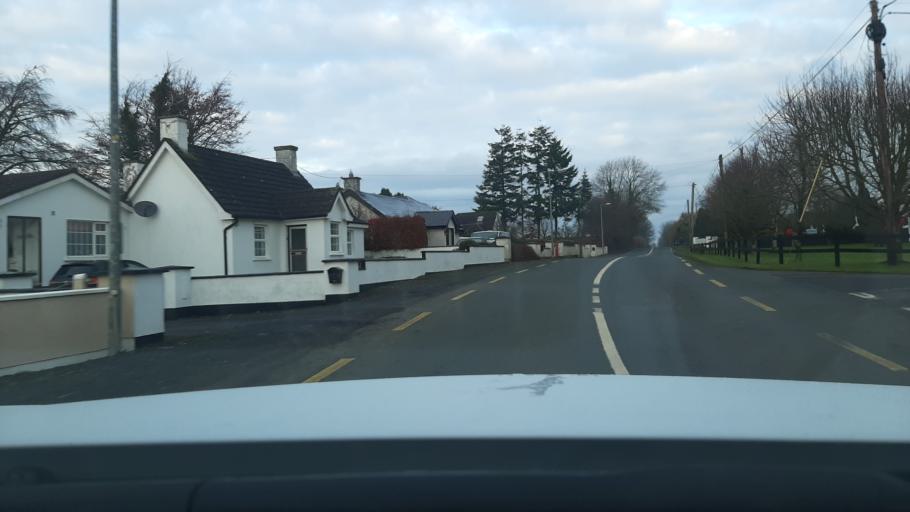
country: IE
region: Leinster
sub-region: Kildare
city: Rathangan
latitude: 53.2344
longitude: -7.0100
